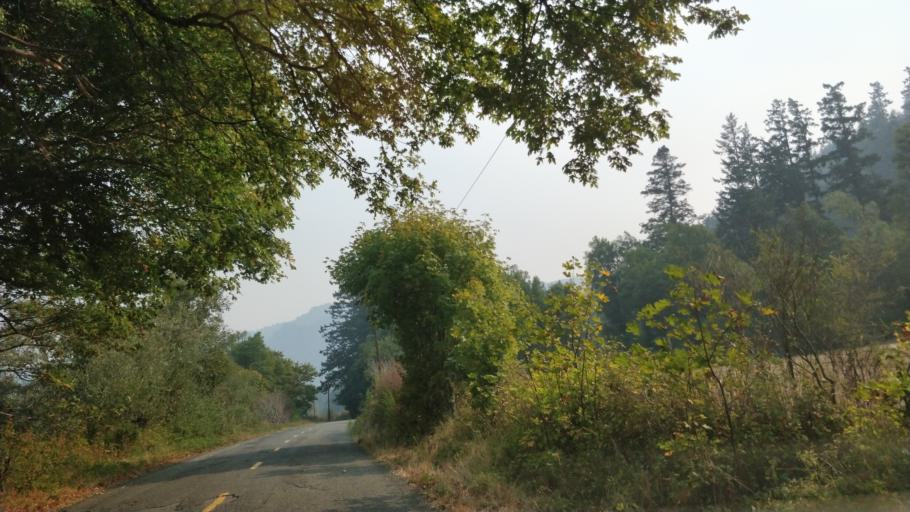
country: US
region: California
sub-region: Humboldt County
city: Rio Dell
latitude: 40.2824
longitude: -124.2498
